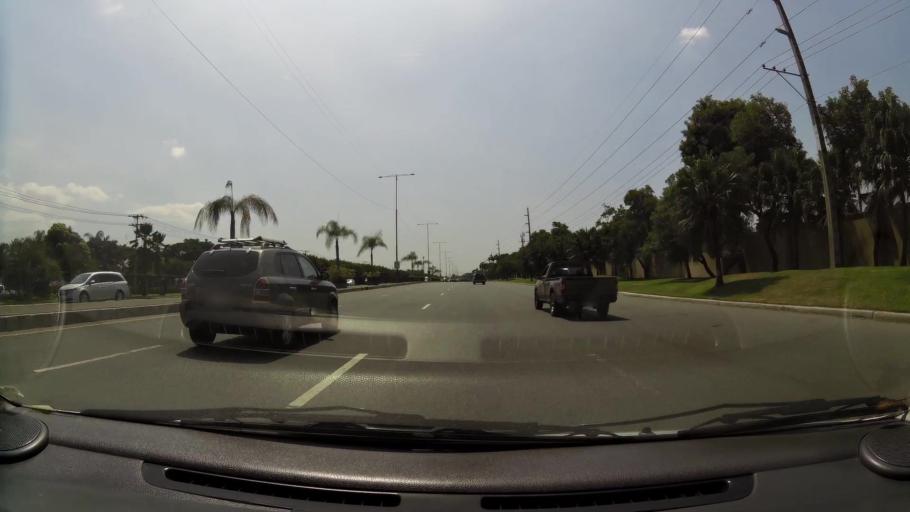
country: EC
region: Guayas
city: Eloy Alfaro
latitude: -2.0955
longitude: -79.8737
